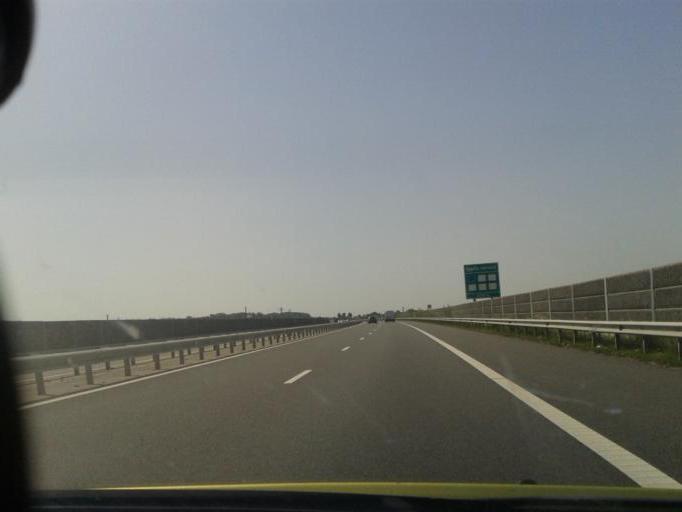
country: RO
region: Prahova
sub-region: Comuna Rafov
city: Rafov
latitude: 44.8750
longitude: 26.1379
